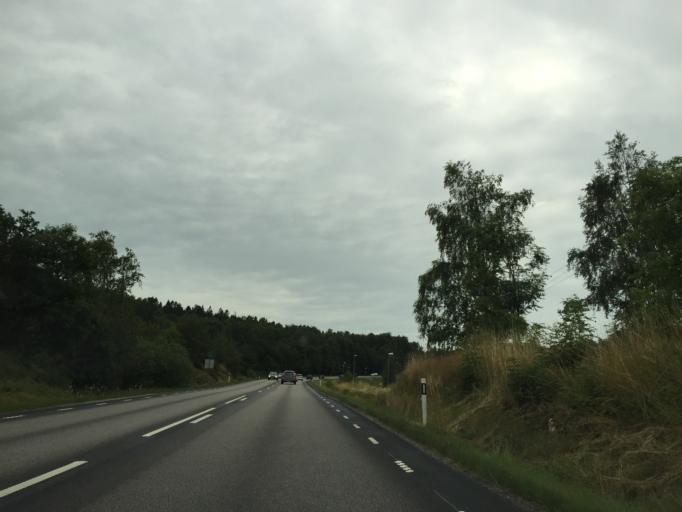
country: SE
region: Vaestra Goetaland
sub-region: Tjorns Kommun
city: Myggenas
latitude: 58.0430
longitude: 11.7428
